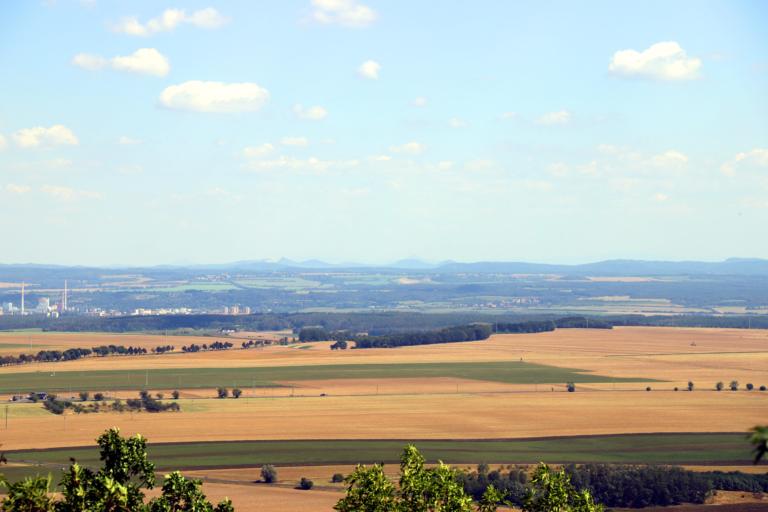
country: CZ
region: Ustecky
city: Roudnice nad Labem
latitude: 50.3880
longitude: 14.2920
